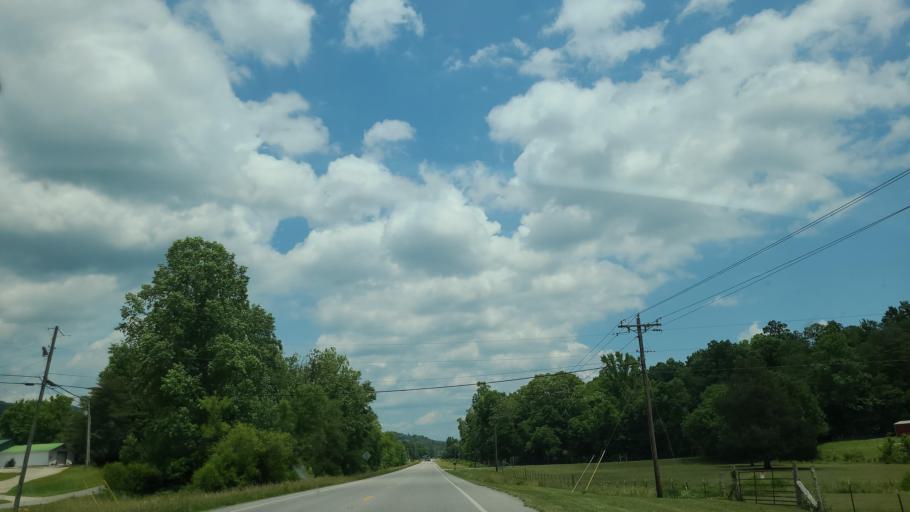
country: US
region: Tennessee
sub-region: Bledsoe County
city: Pikeville
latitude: 35.6398
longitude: -85.1700
